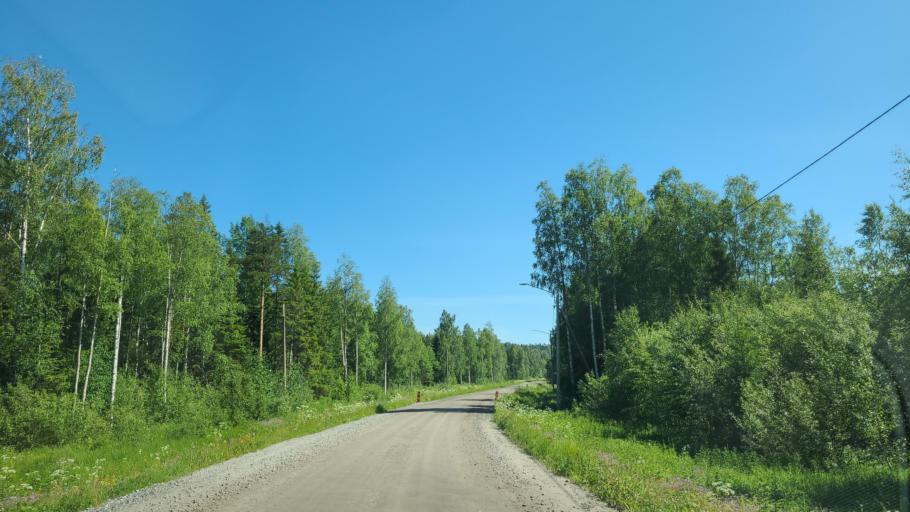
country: SE
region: Vaesterbotten
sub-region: Bjurholms Kommun
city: Bjurholm
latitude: 63.6983
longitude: 18.9483
